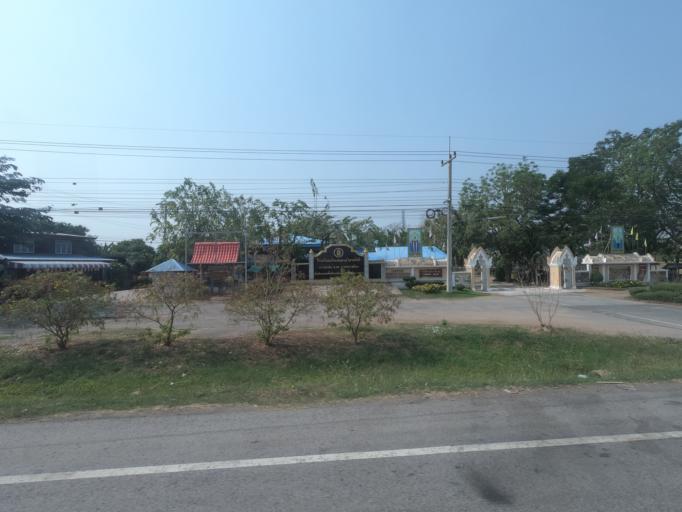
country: TH
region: Nakhon Ratchasima
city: Non Daeng
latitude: 15.3782
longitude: 102.4611
